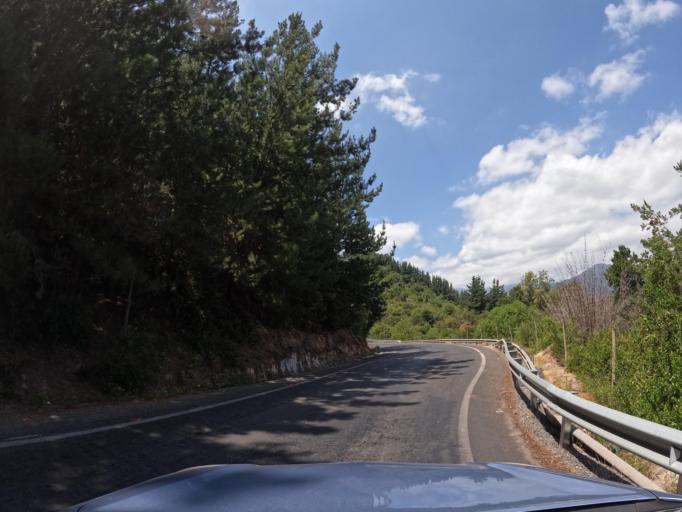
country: CL
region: Maule
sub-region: Provincia de Curico
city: Molina
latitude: -35.1754
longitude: -71.1017
